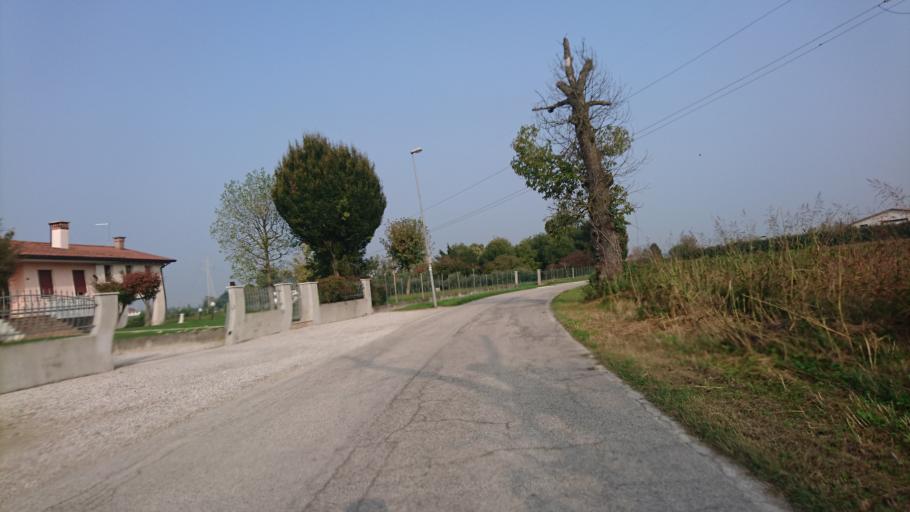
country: IT
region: Veneto
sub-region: Provincia di Padova
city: Santa Maria di Non
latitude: 45.5063
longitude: 11.8497
